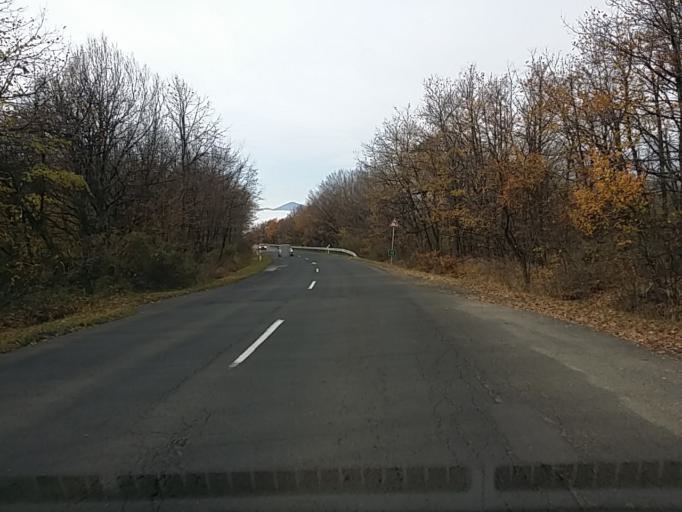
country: HU
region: Heves
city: Gyongyossolymos
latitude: 47.8519
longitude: 19.9627
